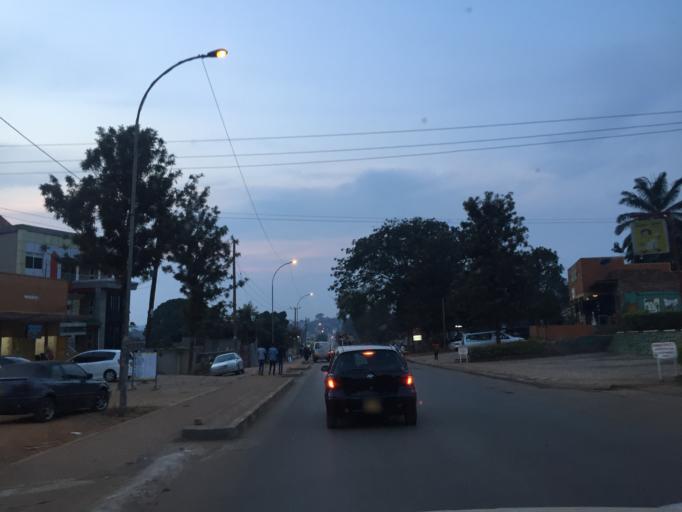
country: UG
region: Central Region
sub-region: Kampala District
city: Kampala
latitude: 0.2740
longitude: 32.6167
